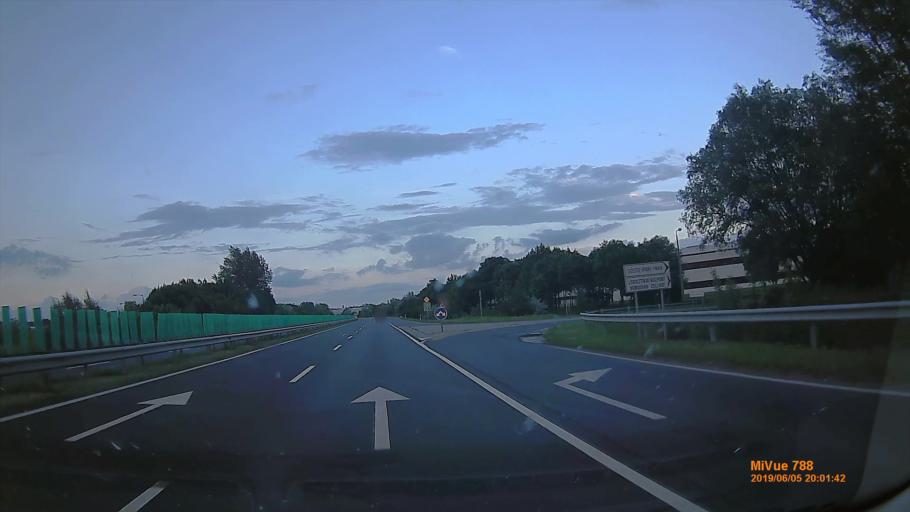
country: HU
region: Fejer
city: Szekesfehervar
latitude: 47.1473
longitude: 18.4143
